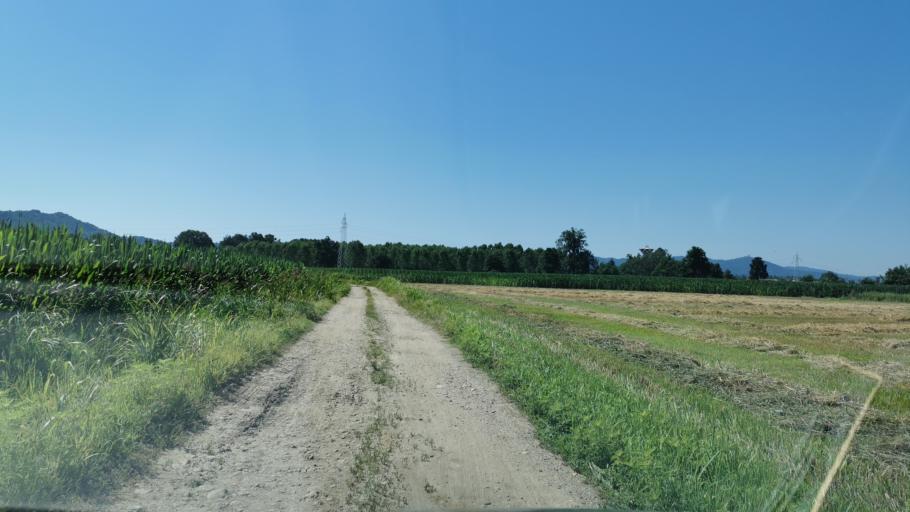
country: IT
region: Piedmont
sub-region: Provincia di Torino
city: Brandizzo
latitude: 45.1921
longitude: 7.8331
